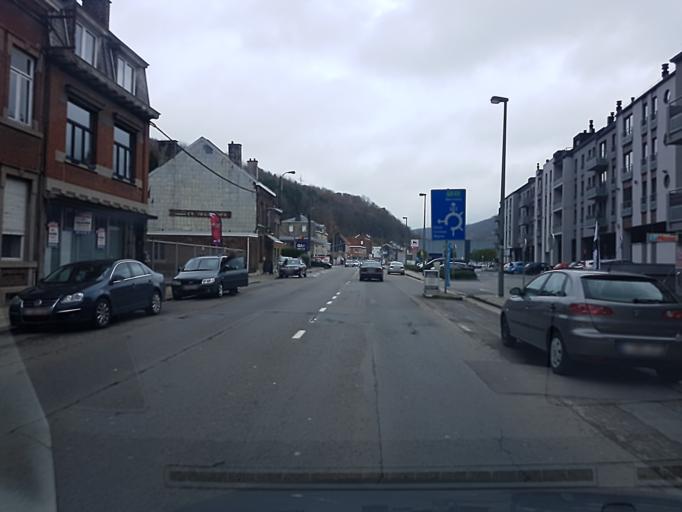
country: BE
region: Wallonia
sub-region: Province de Liege
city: Pepinster
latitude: 50.5698
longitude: 5.8072
